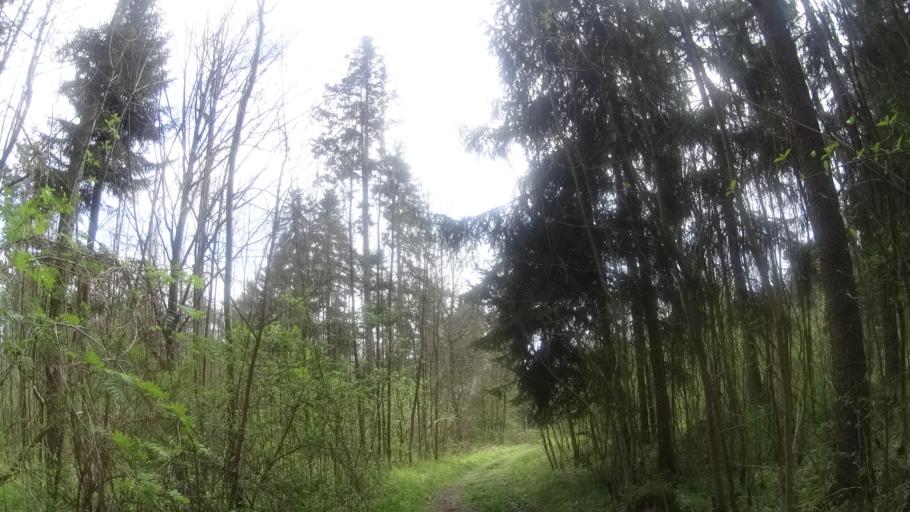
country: DE
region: Bavaria
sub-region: Upper Franconia
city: Igensdorf
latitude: 49.6268
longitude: 11.2035
